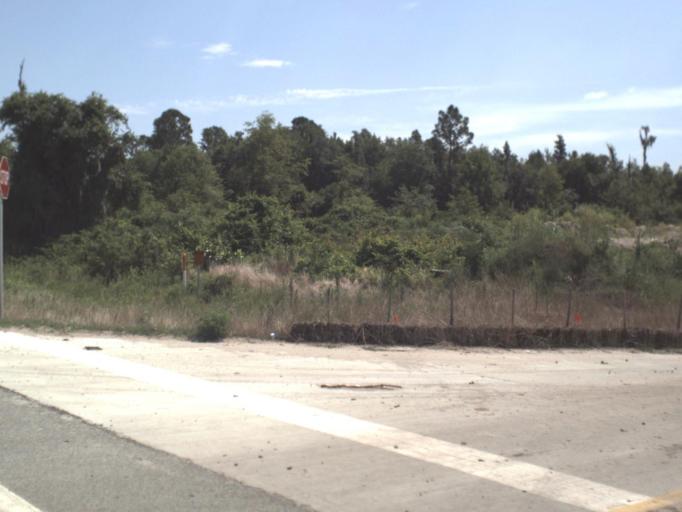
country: US
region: Florida
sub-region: Hamilton County
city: Jasper
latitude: 30.4637
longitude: -82.9313
